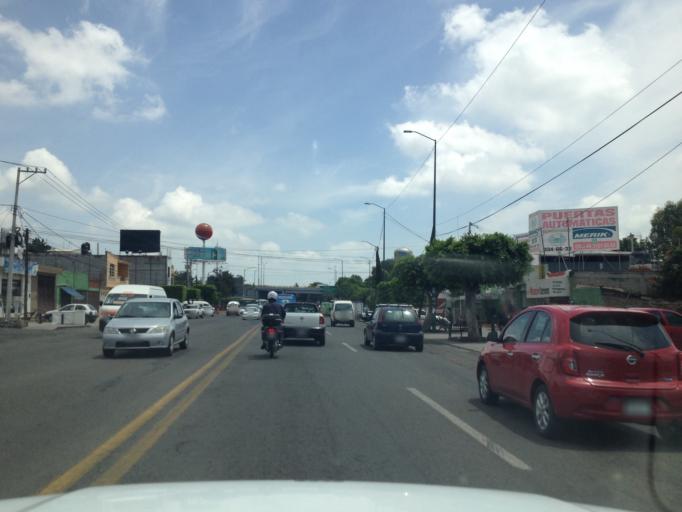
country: MX
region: Michoacan
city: Morelia
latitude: 19.7189
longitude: -101.1885
